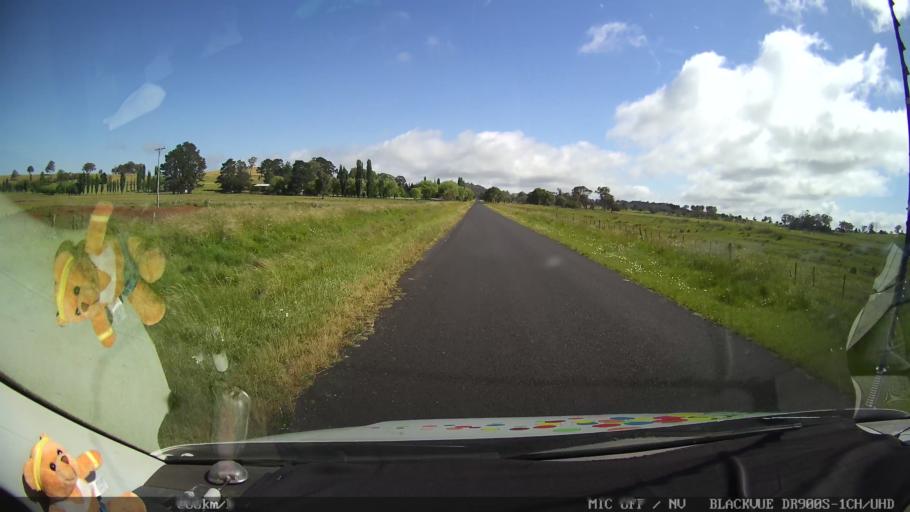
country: AU
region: New South Wales
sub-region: Guyra
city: Guyra
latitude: -30.0509
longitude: 151.6659
